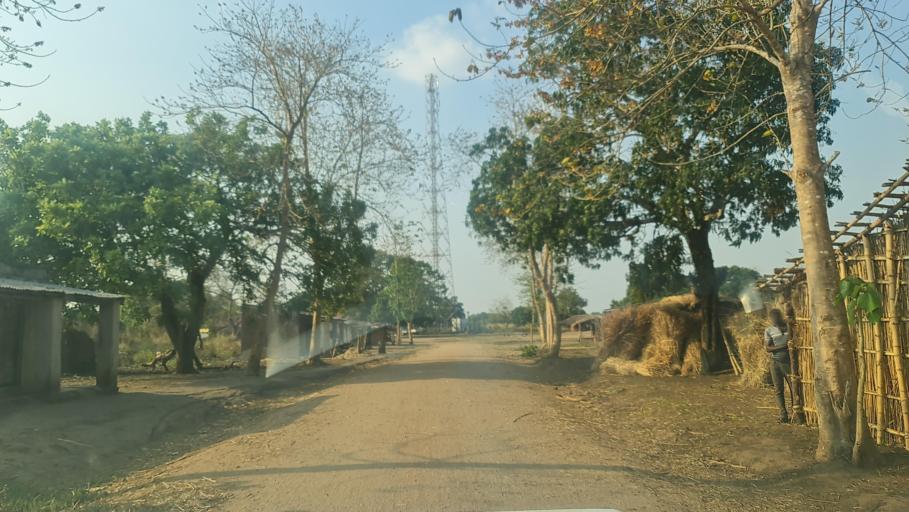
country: MZ
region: Zambezia
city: Quelimane
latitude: -18.1447
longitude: 35.9868
